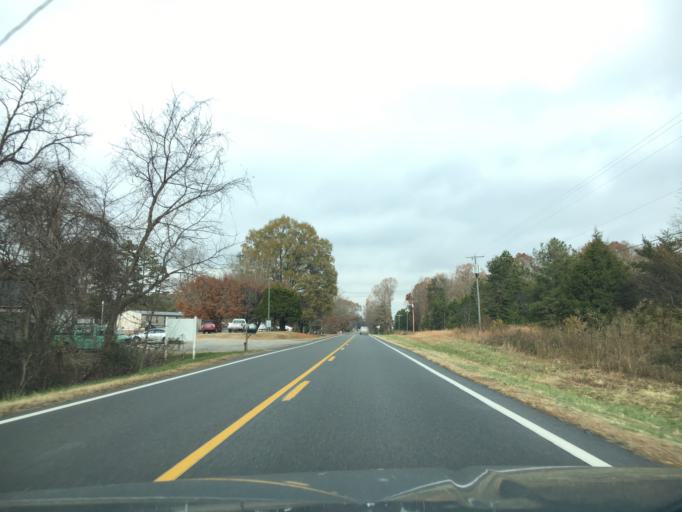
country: US
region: Virginia
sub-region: Prince Edward County
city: Farmville
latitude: 37.3507
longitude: -78.3815
